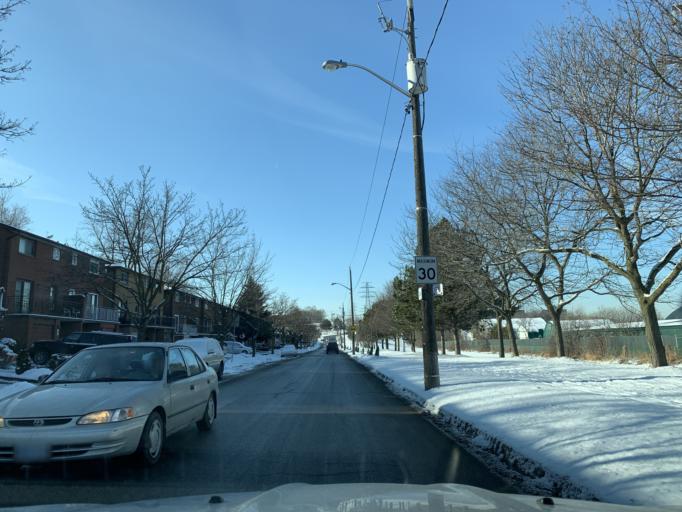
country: CA
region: Ontario
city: Toronto
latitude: 43.6734
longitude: -79.4827
